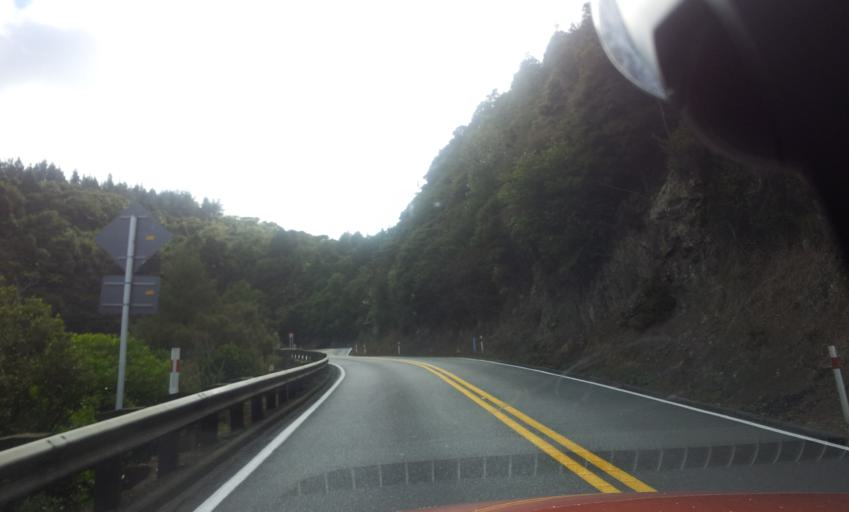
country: NZ
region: Northland
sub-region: Whangarei
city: Ruakaka
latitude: -36.0745
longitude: 174.4195
